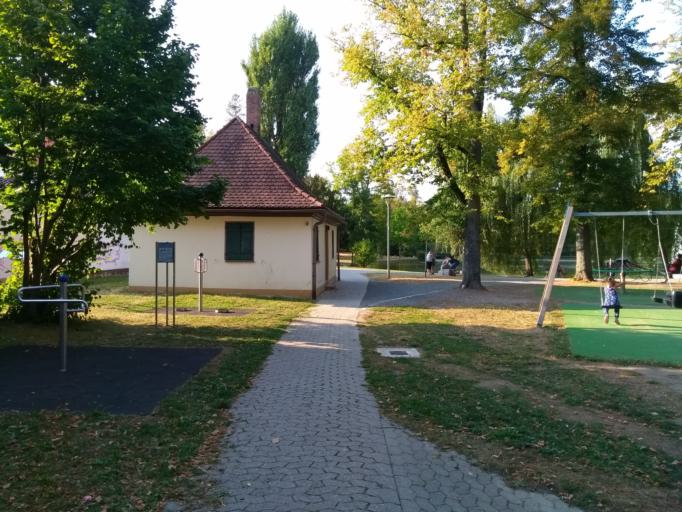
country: DE
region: Bavaria
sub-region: Regierungsbezirk Mittelfranken
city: Neustadt an der Aisch
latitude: 49.5795
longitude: 10.6048
